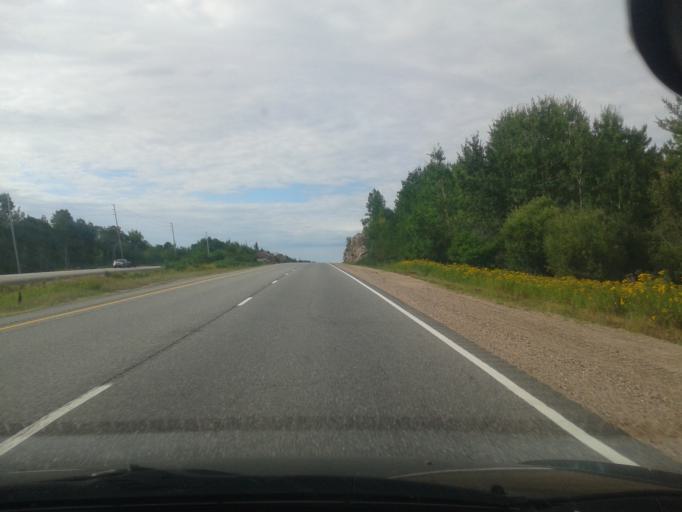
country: CA
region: Ontario
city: Powassan
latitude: 46.1593
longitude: -79.3594
